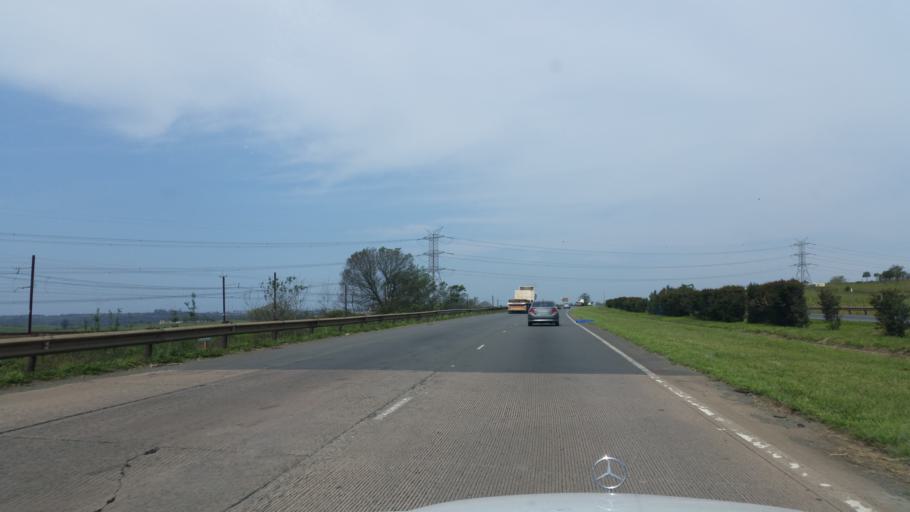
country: ZA
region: KwaZulu-Natal
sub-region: uMgungundlovu District Municipality
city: Camperdown
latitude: -29.7306
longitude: 30.5631
